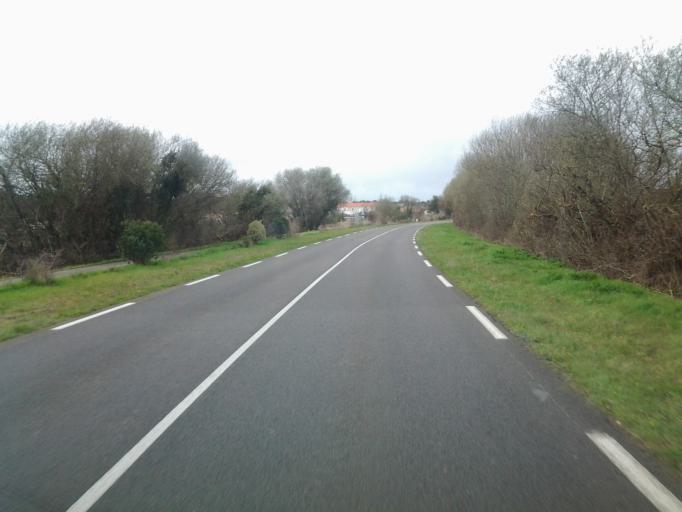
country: FR
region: Pays de la Loire
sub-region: Departement de la Vendee
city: La Tranche-sur-Mer
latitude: 46.3644
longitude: -1.4553
